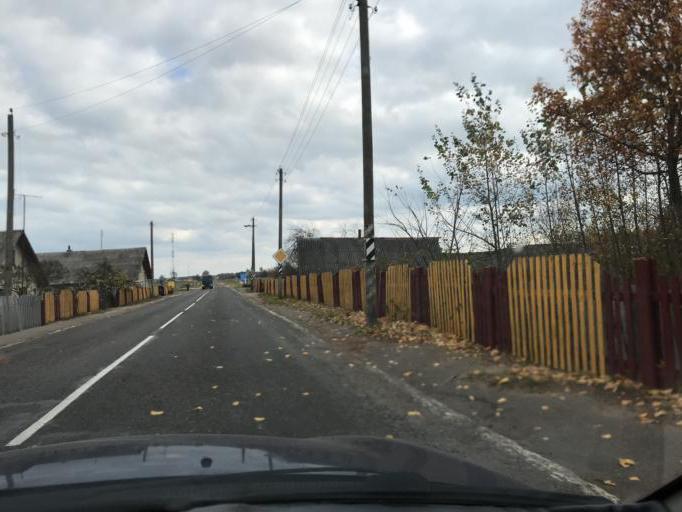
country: BY
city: Berezovka
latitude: 53.7410
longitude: 25.3593
